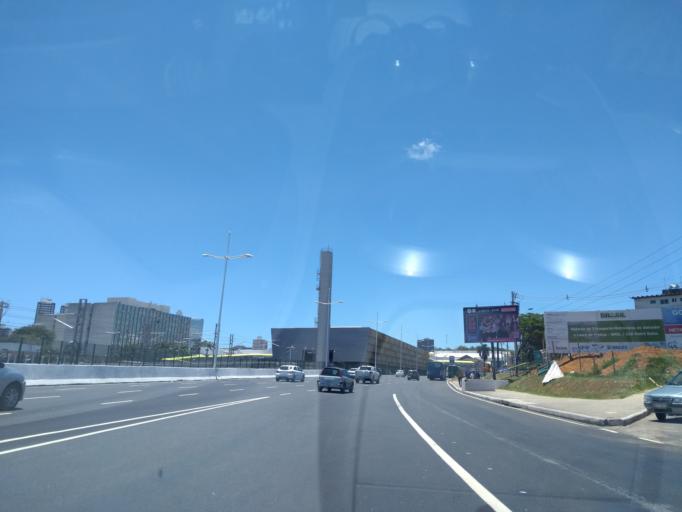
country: BR
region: Bahia
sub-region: Salvador
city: Salvador
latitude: -12.9769
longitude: -38.4621
